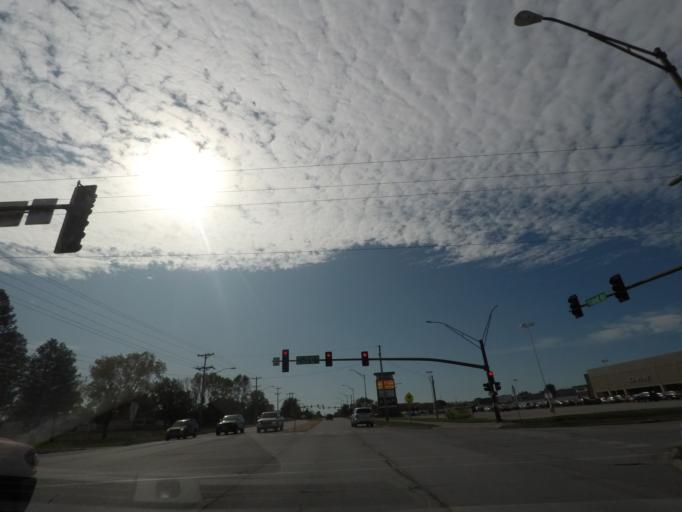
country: US
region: Iowa
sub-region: Story County
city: Ames
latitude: 42.0516
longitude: -93.6203
